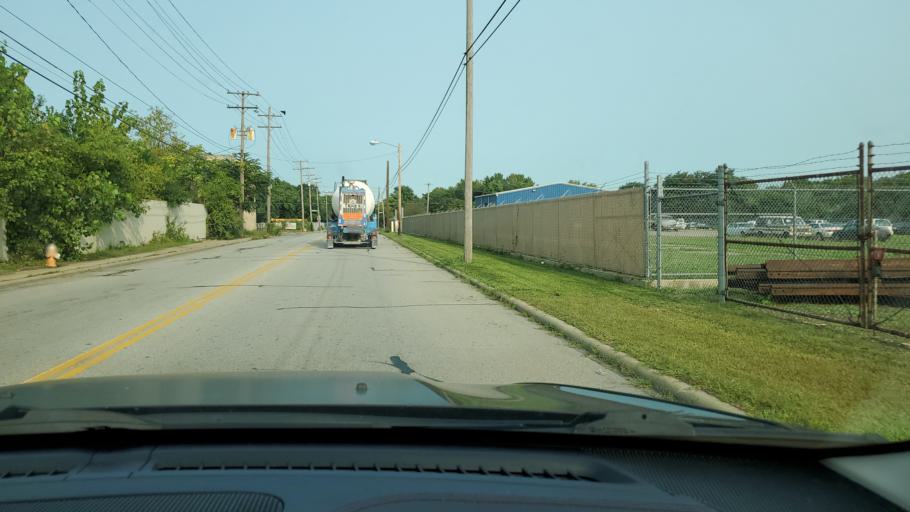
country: US
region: Ohio
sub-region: Mahoning County
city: Youngstown
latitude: 41.0816
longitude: -80.6311
